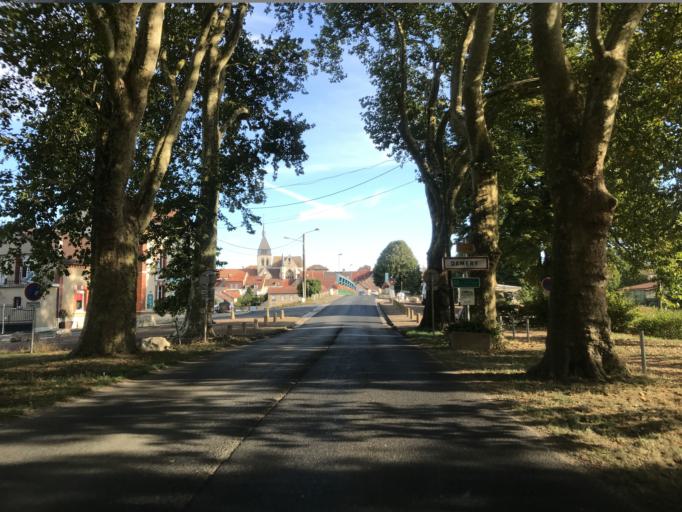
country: FR
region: Champagne-Ardenne
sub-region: Departement de la Marne
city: Damery
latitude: 49.0683
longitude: 3.8767
